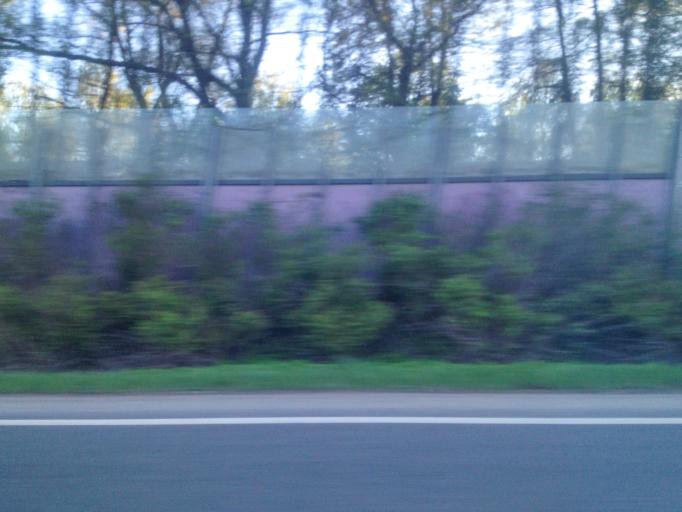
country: FI
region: Haeme
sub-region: Haemeenlinna
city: Haemeenlinna
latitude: 60.9898
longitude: 24.4590
